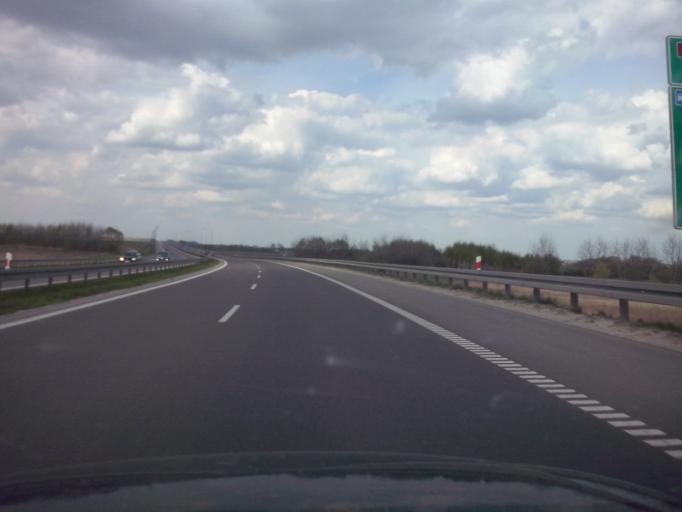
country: PL
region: Subcarpathian Voivodeship
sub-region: Powiat rzeszowski
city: Trzebownisko
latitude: 50.0805
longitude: 22.0609
